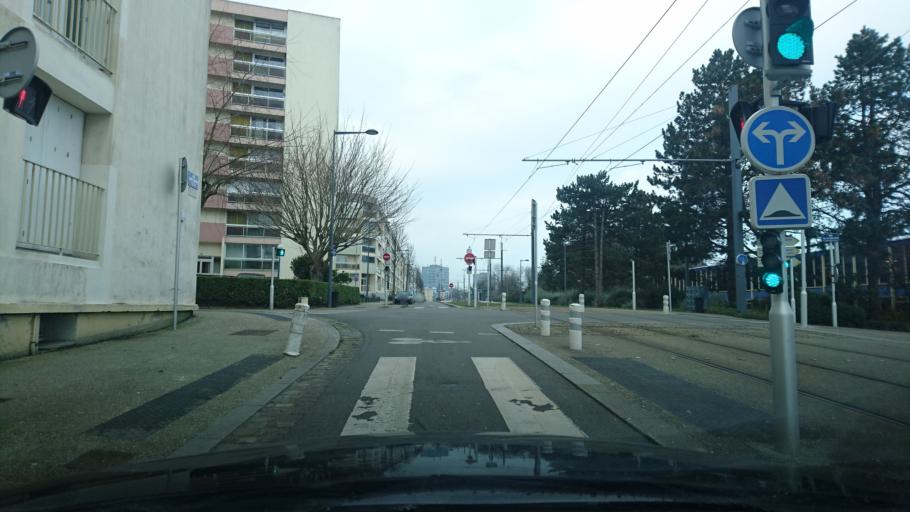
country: FR
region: Brittany
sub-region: Departement du Finistere
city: Brest
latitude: 48.3860
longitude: -4.5042
